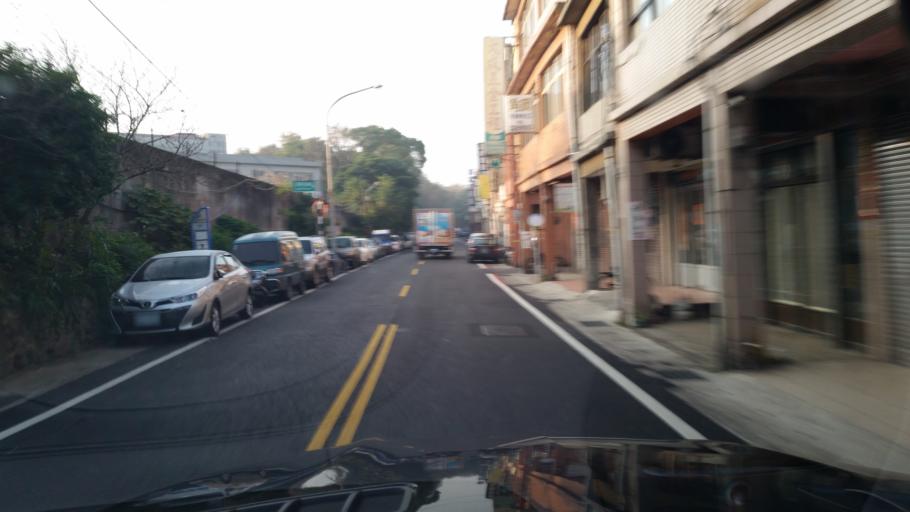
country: TW
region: Taiwan
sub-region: Taoyuan
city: Taoyuan
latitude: 25.0622
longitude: 121.3599
